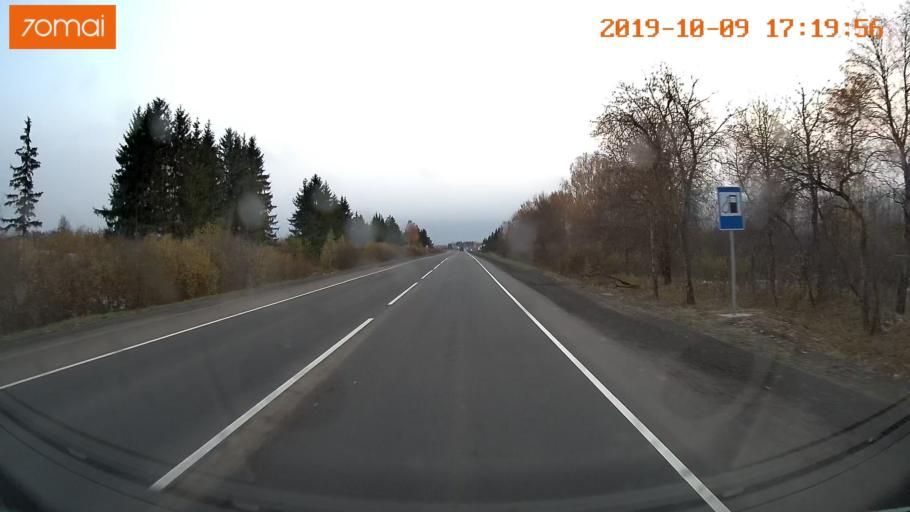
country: RU
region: Ivanovo
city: Furmanov
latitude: 57.2402
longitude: 41.1470
